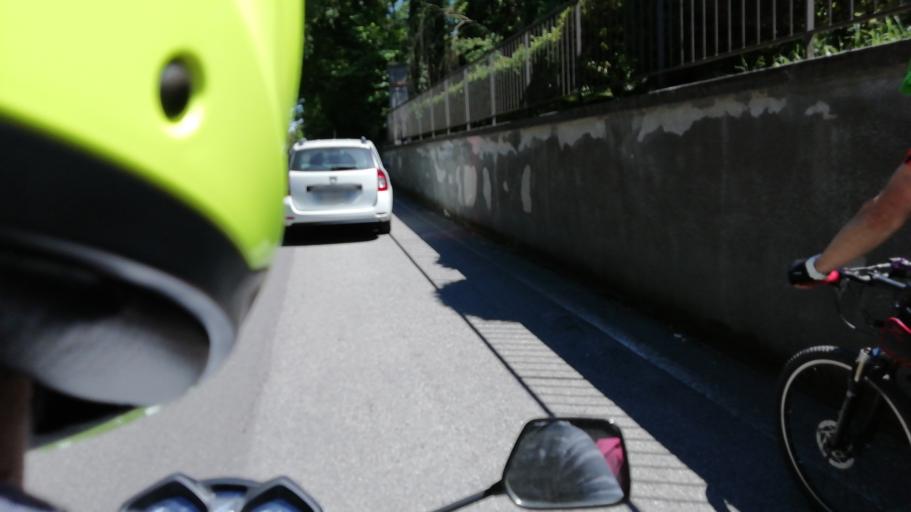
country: IT
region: Lombardy
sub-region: Provincia di Varese
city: Ferno
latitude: 45.6158
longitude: 8.7442
